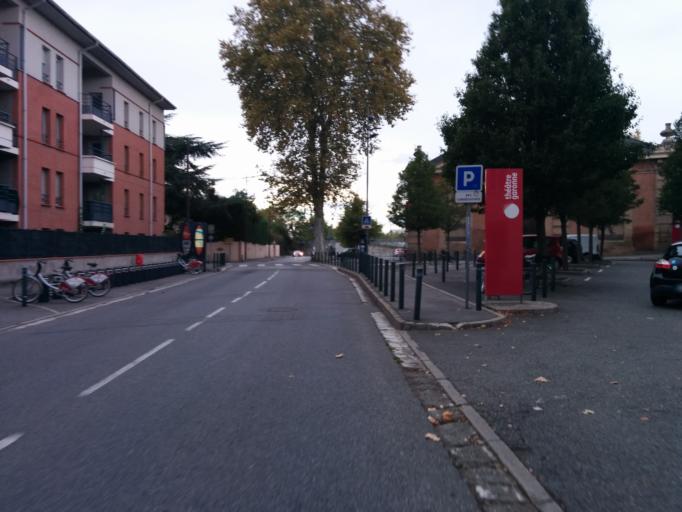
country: FR
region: Midi-Pyrenees
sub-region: Departement de la Haute-Garonne
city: Toulouse
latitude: 43.6023
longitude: 1.4257
